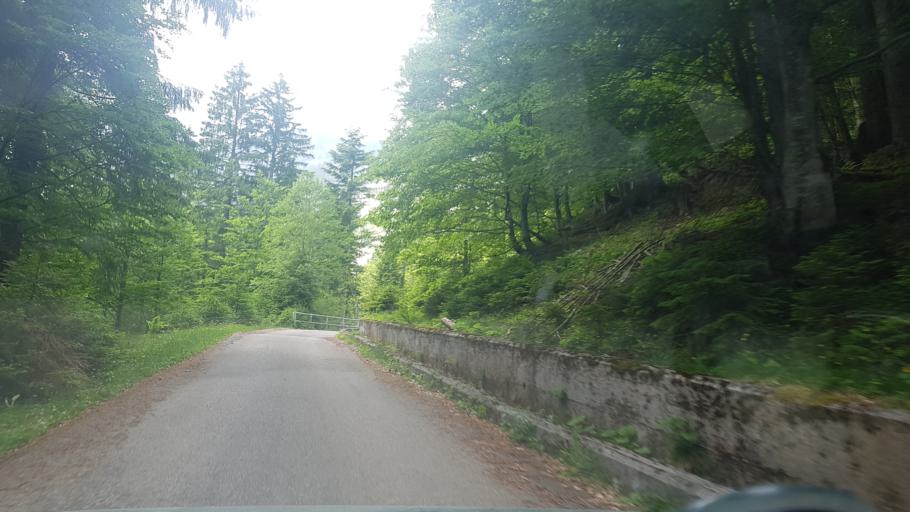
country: IT
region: Friuli Venezia Giulia
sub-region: Provincia di Udine
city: Paularo
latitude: 46.5459
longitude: 13.2046
